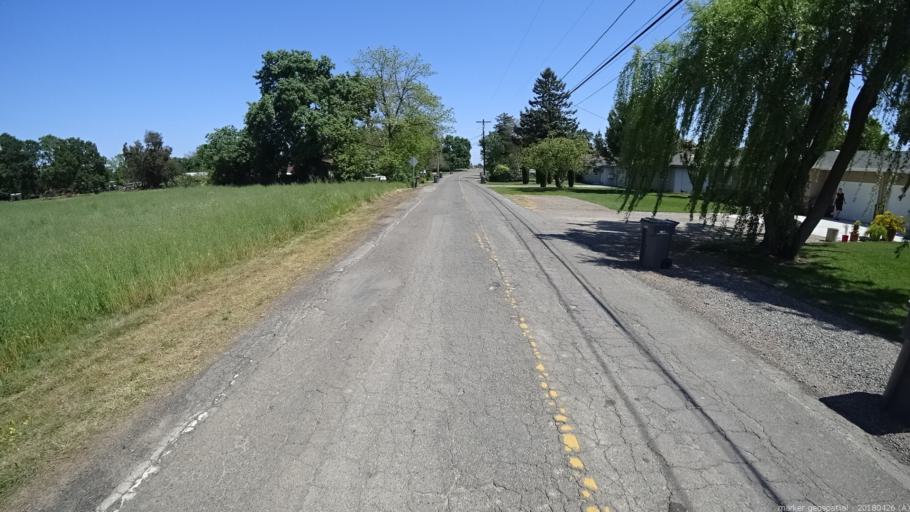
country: US
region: California
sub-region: Yolo County
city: West Sacramento
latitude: 38.5323
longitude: -121.5463
